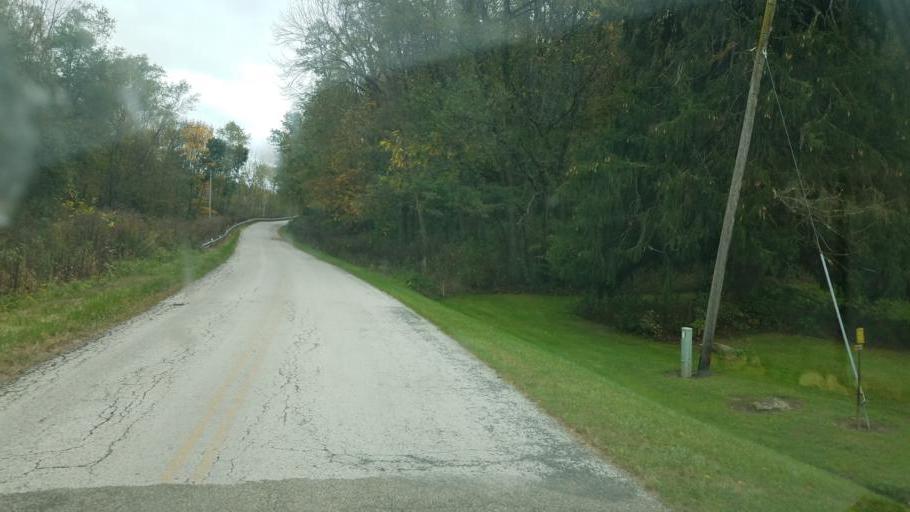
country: US
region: Ohio
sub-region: Ashland County
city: Loudonville
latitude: 40.5796
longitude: -82.1677
